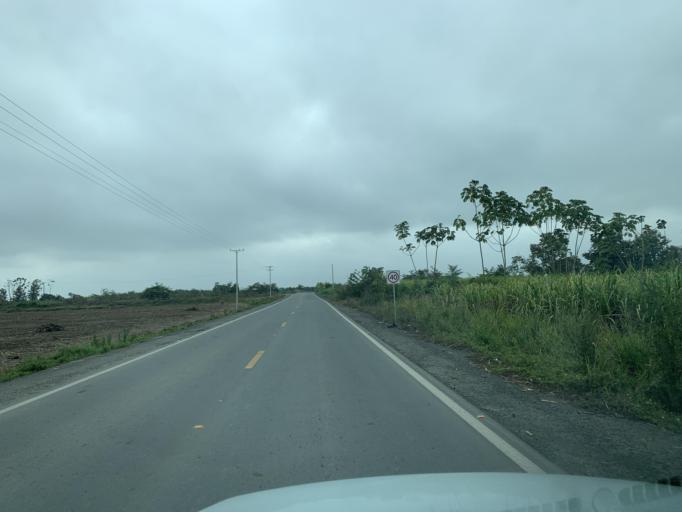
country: EC
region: Guayas
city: Coronel Marcelino Mariduena
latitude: -2.3059
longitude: -79.5037
